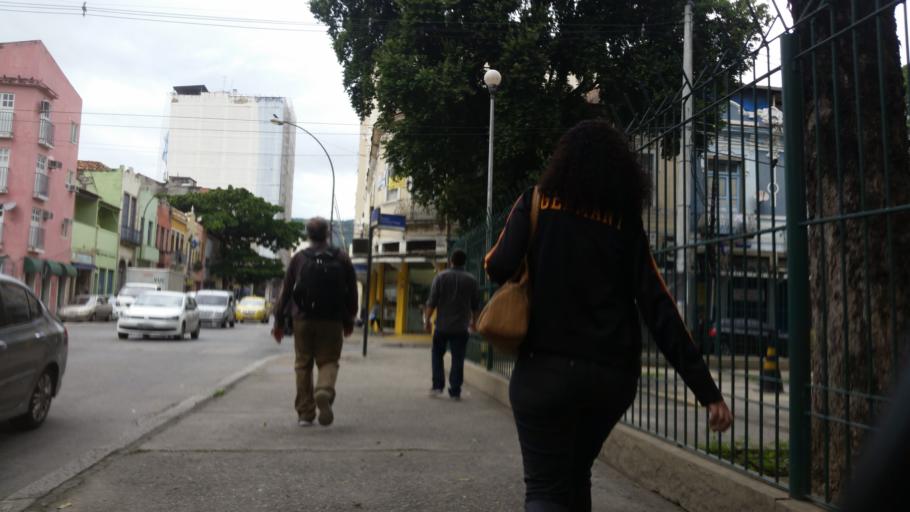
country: BR
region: Rio de Janeiro
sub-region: Rio De Janeiro
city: Rio de Janeiro
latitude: -22.9077
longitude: -43.1942
